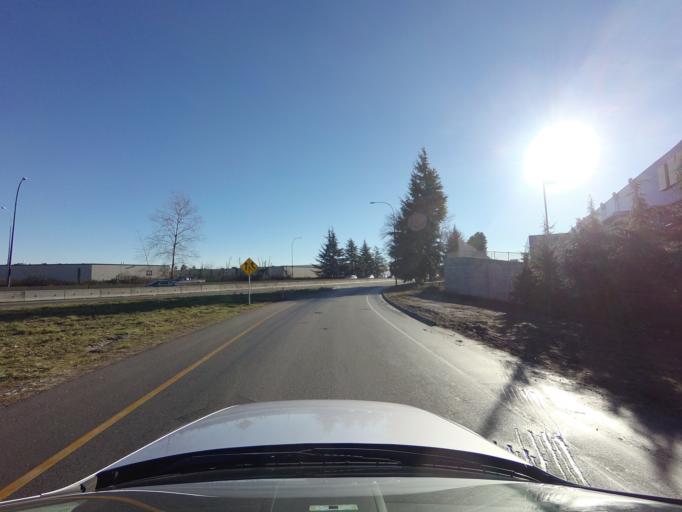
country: CA
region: British Columbia
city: Richmond
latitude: 49.1902
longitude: -123.0783
